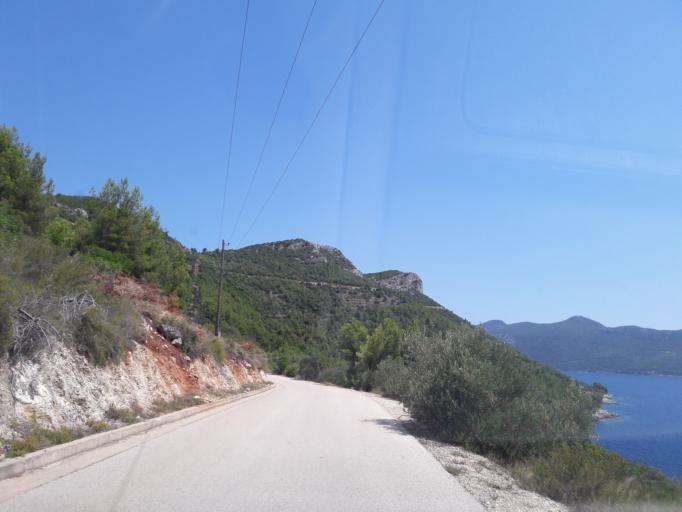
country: HR
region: Dubrovacko-Neretvanska
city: Blato
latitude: 42.9128
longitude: 17.4165
